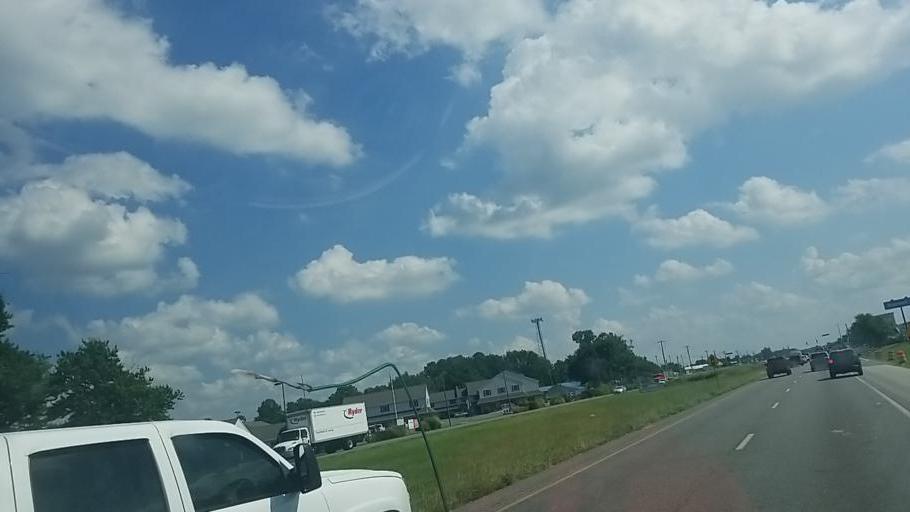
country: US
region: Delaware
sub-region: Sussex County
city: Georgetown
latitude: 38.7045
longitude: -75.4028
